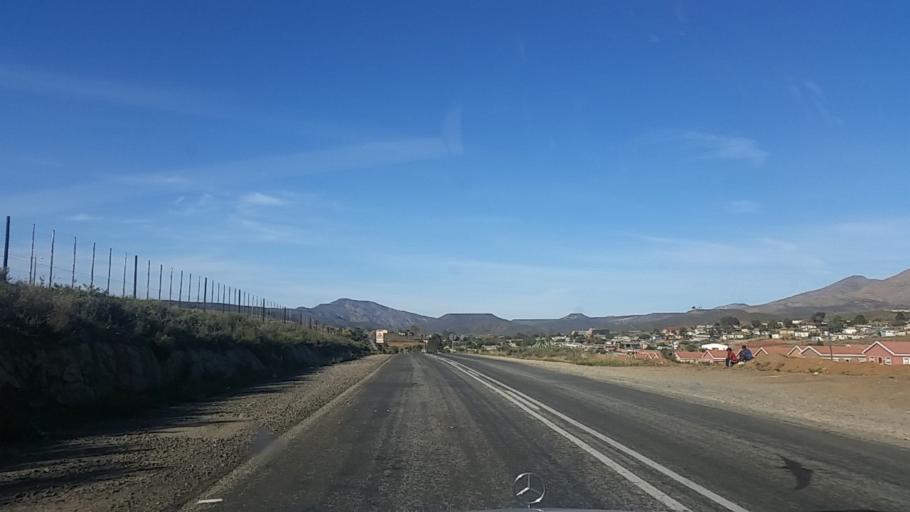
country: ZA
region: Western Cape
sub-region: Eden District Municipality
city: Knysna
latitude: -33.6652
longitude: 23.1046
